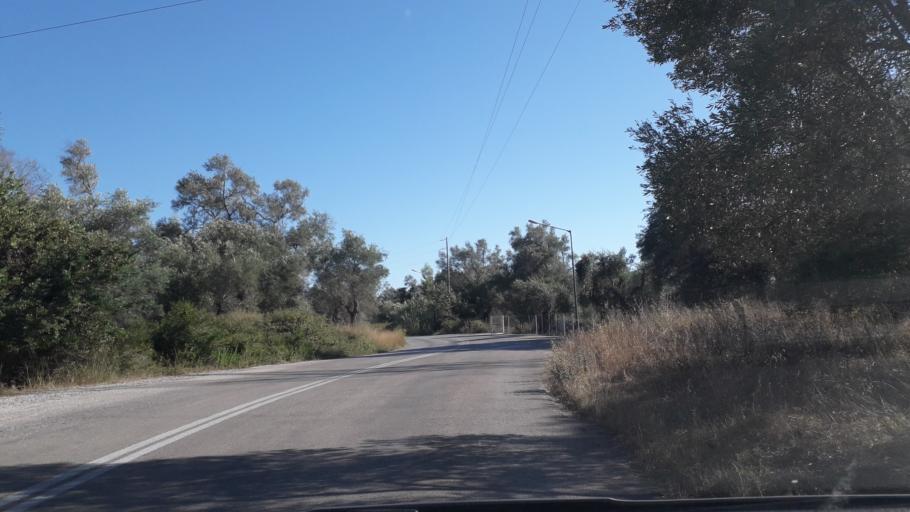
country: GR
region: Ionian Islands
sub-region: Nomos Kerkyras
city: Perivoli
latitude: 39.4416
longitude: 19.9532
